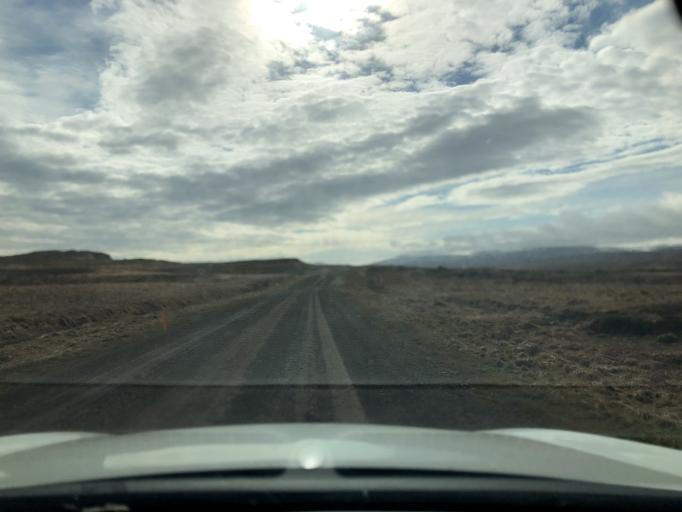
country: IS
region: West
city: Borgarnes
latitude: 65.0197
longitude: -22.0583
